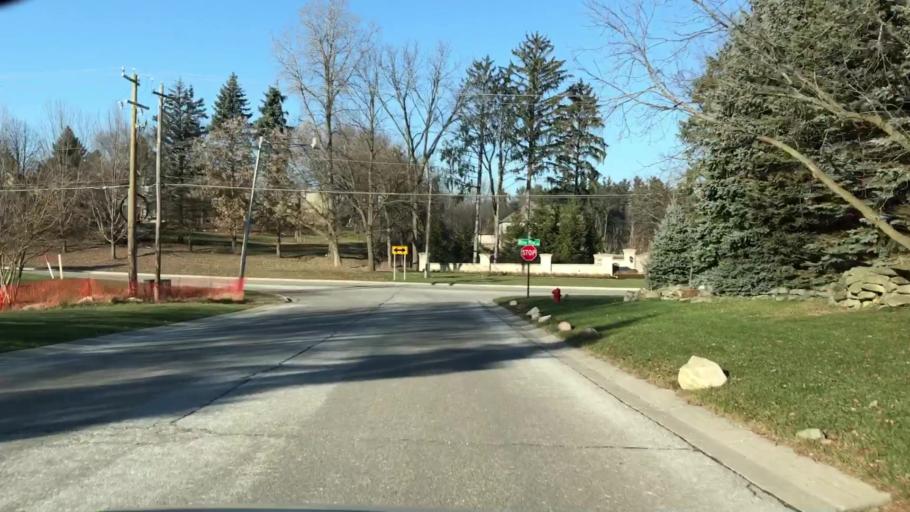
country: US
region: Michigan
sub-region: Wayne County
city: Northville
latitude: 42.4514
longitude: -83.4840
